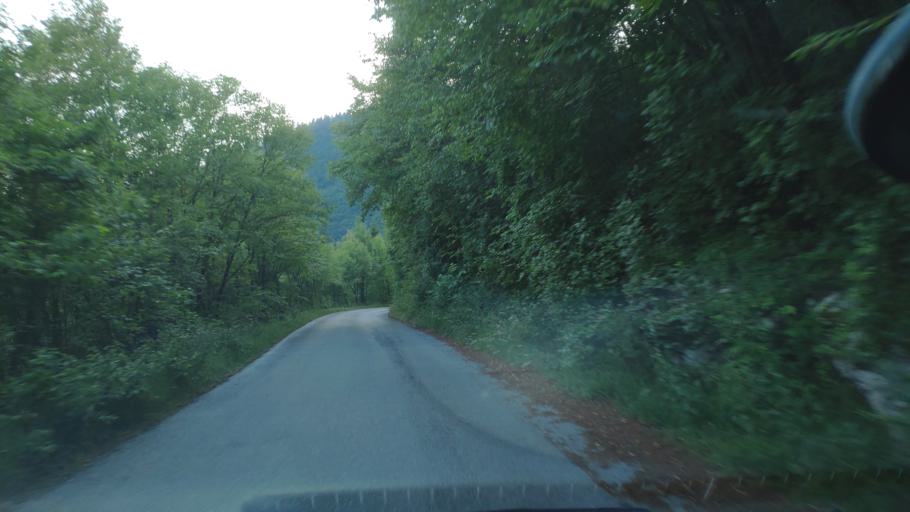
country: IT
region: Veneto
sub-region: Provincia di Vicenza
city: Calvene
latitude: 45.7860
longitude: 11.5118
